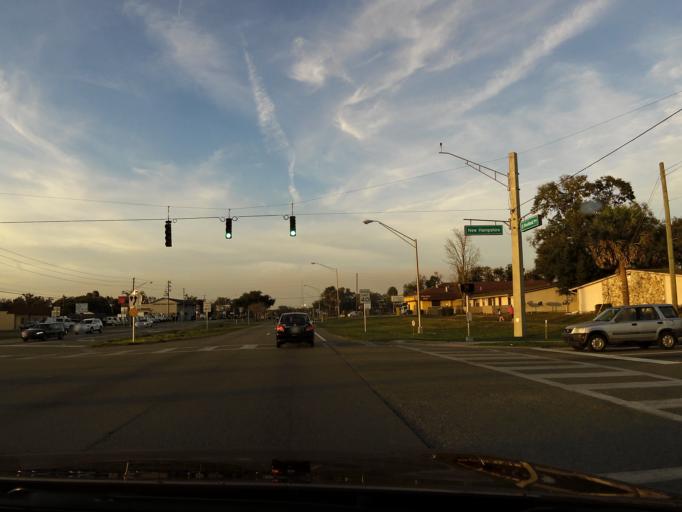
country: US
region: Florida
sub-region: Volusia County
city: De Land Southwest
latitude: 29.0061
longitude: -81.3026
